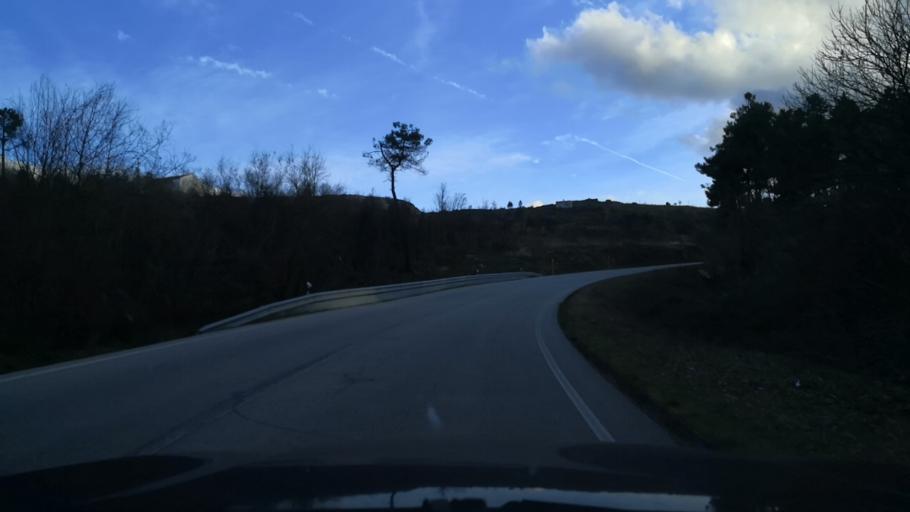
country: PT
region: Braganca
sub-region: Carrazeda de Ansiaes
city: Carrazeda de Anciaes
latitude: 41.2541
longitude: -7.3161
